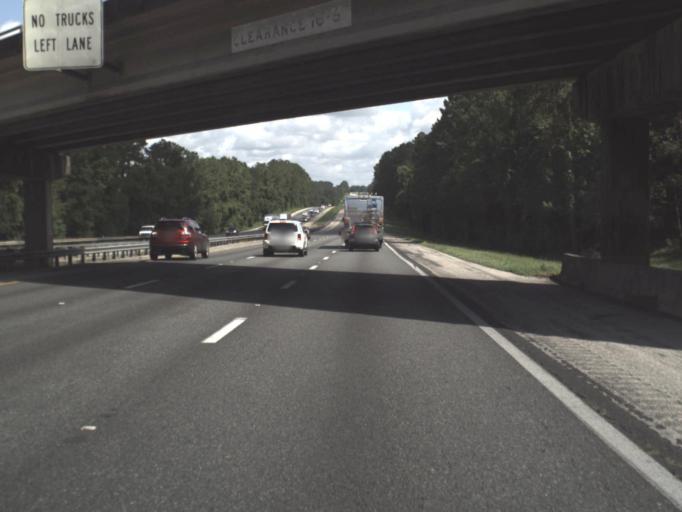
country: US
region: Florida
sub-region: Alachua County
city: Alachua
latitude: 29.7160
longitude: -82.4656
